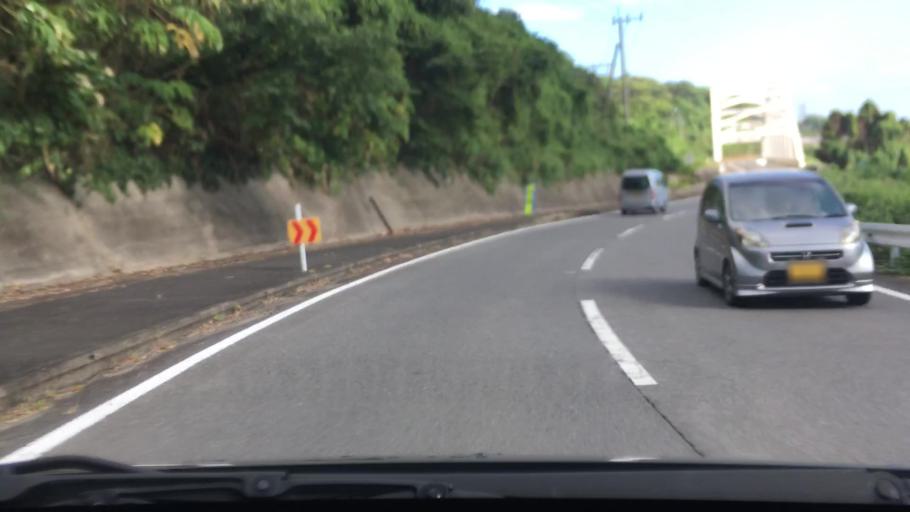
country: JP
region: Nagasaki
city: Togitsu
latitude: 32.8589
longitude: 129.6855
